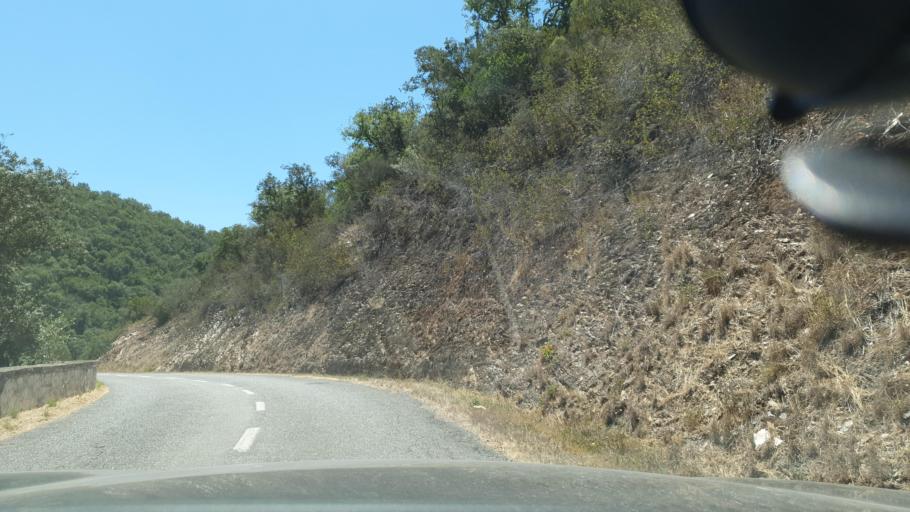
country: PT
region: Beja
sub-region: Odemira
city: Odemira
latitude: 37.6021
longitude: -8.5896
